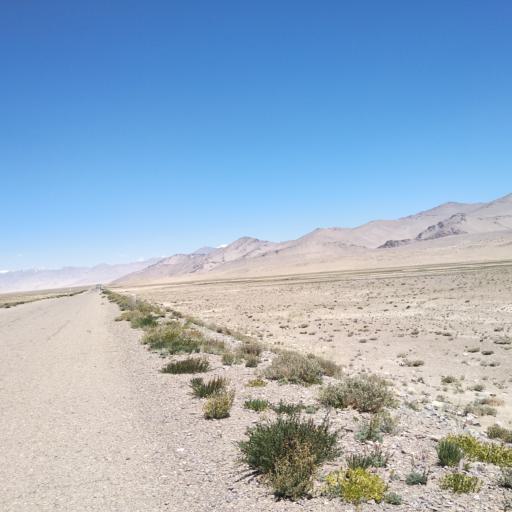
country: TJ
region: Gorno-Badakhshan
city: Murghob
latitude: 38.8999
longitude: 73.4974
